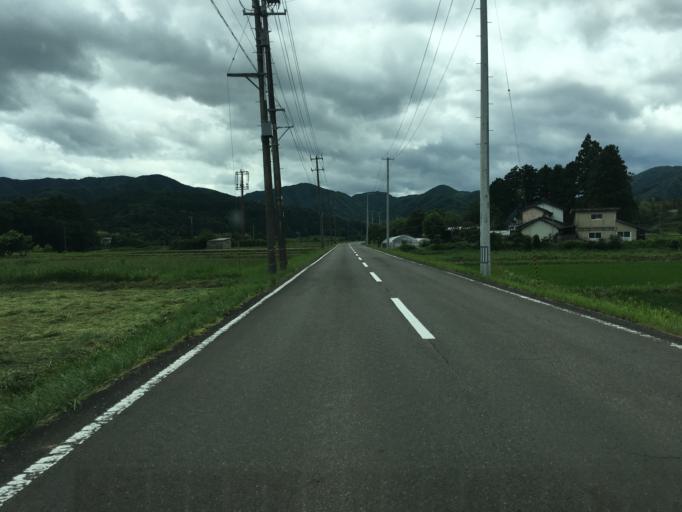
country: JP
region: Miyagi
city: Marumori
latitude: 37.7255
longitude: 140.8910
